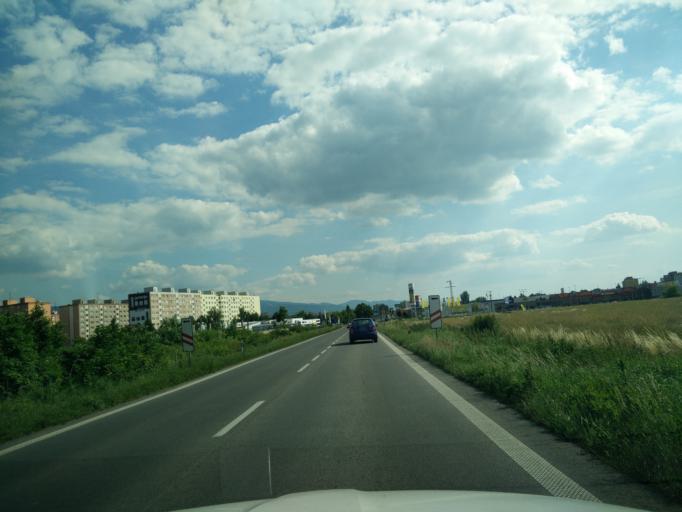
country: SK
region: Nitriansky
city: Prievidza
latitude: 48.7888
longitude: 18.6301
